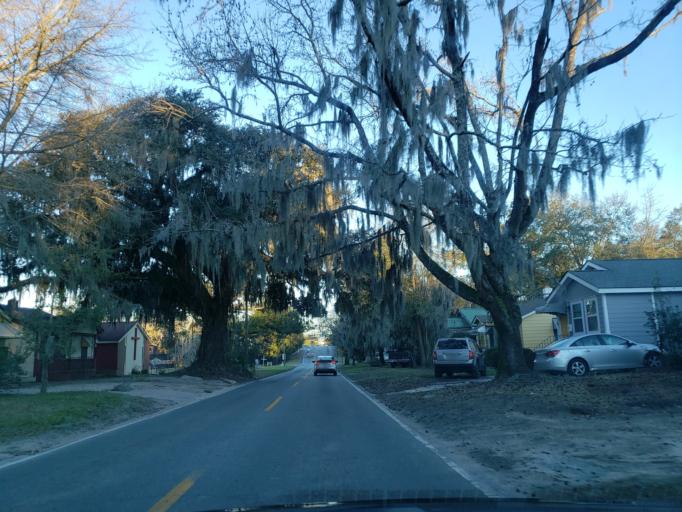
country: US
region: Georgia
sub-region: Chatham County
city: Thunderbolt
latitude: 32.0356
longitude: -81.0873
